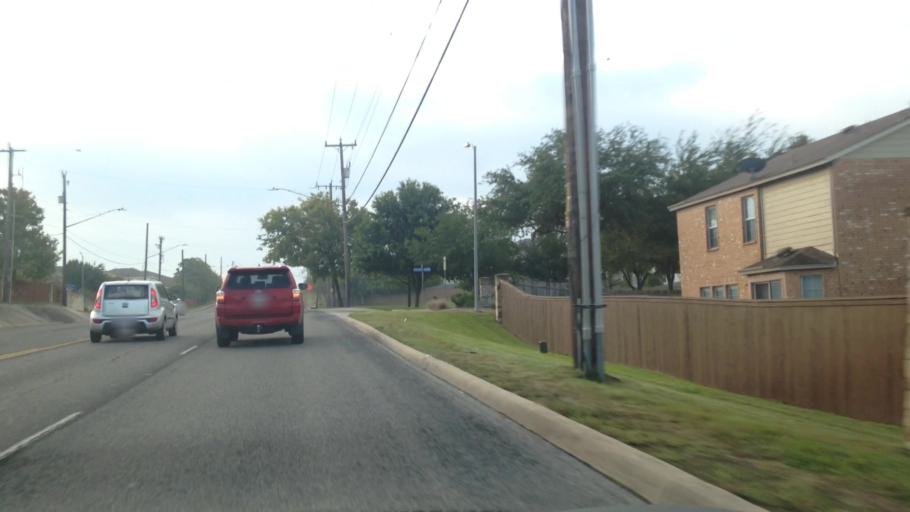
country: US
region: Texas
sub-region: Bexar County
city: Live Oak
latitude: 29.5588
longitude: -98.3599
